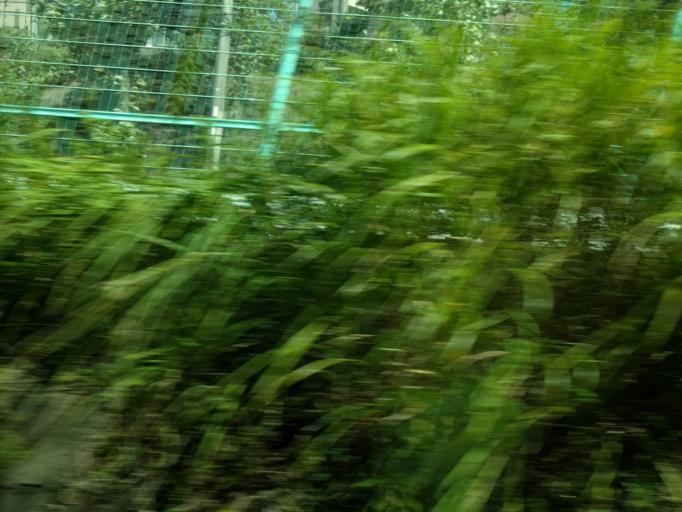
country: JP
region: Tokyo
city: Chofugaoka
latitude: 35.6065
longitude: 139.5970
